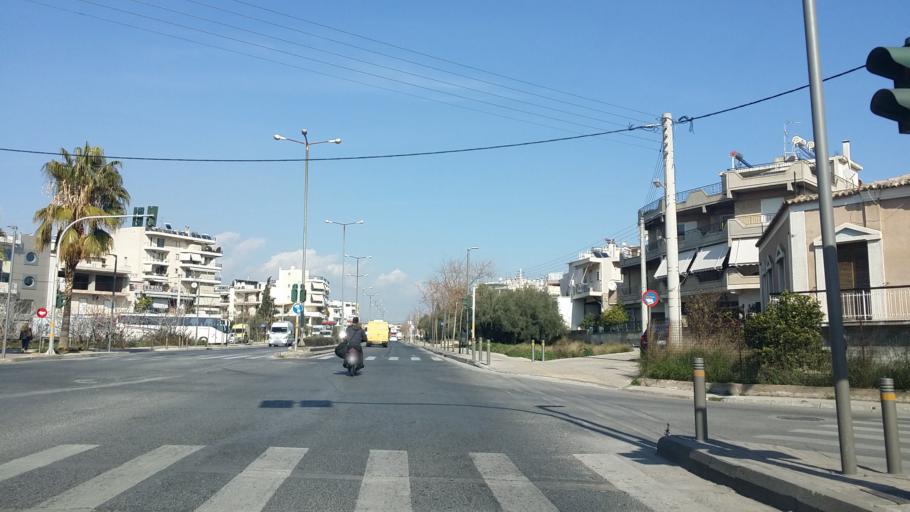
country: GR
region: Attica
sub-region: Nomarchia Athinas
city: Ilion
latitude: 38.0341
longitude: 23.7030
